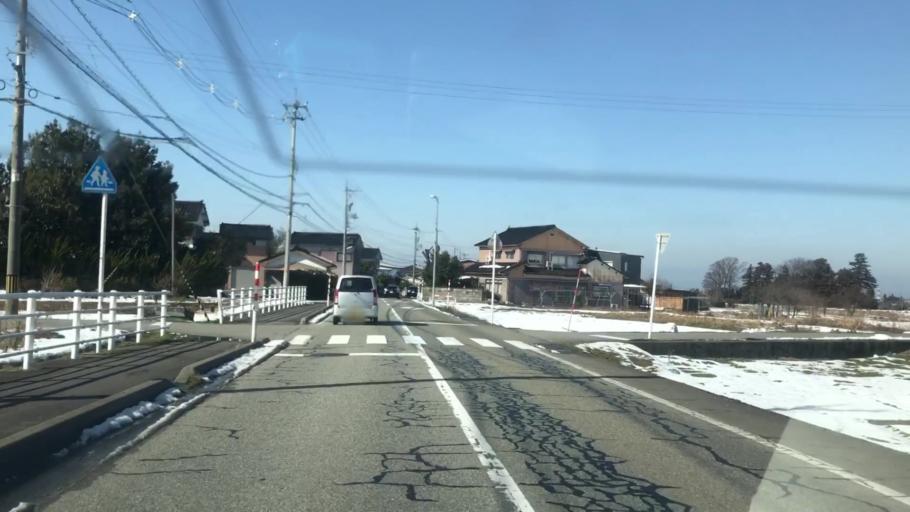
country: JP
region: Toyama
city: Toyama-shi
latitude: 36.6430
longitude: 137.2555
